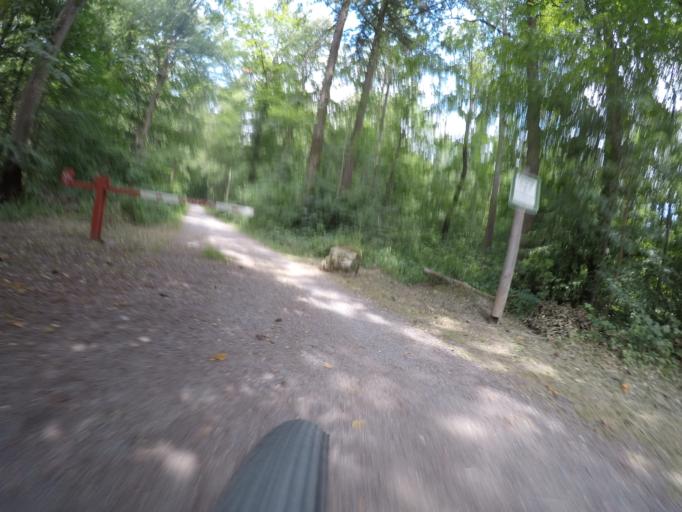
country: DE
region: Baden-Wuerttemberg
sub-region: Regierungsbezirk Stuttgart
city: Gerlingen
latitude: 48.7818
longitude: 9.0902
